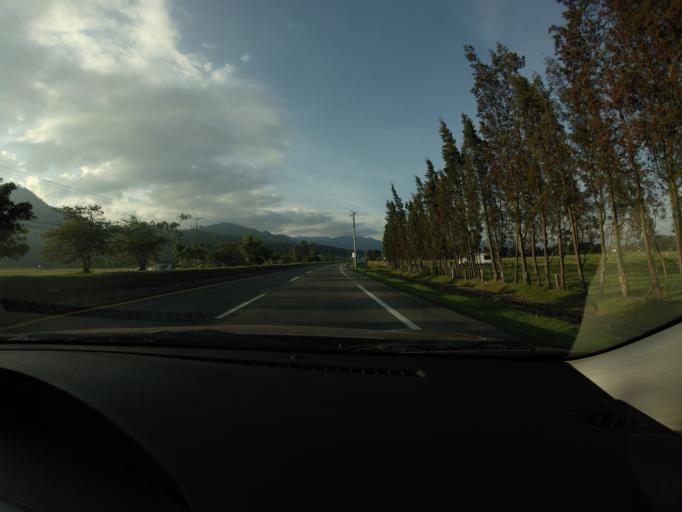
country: CO
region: Cundinamarca
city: Zipaquira
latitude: 5.0062
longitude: -74.0049
